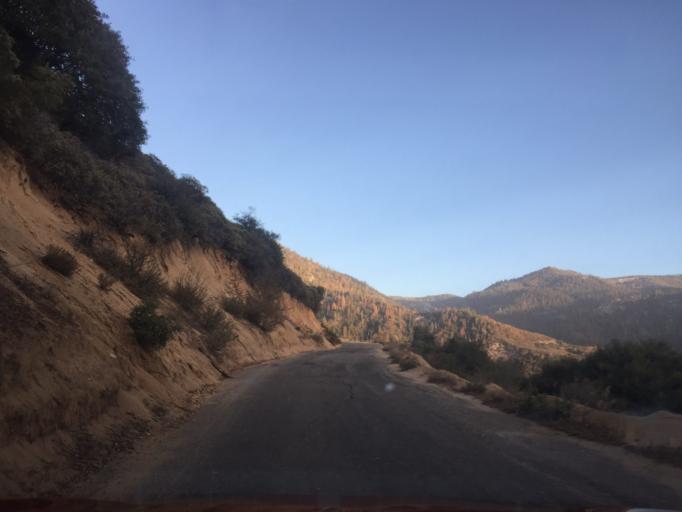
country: US
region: California
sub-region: Tulare County
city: Three Rivers
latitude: 36.4378
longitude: -118.7229
